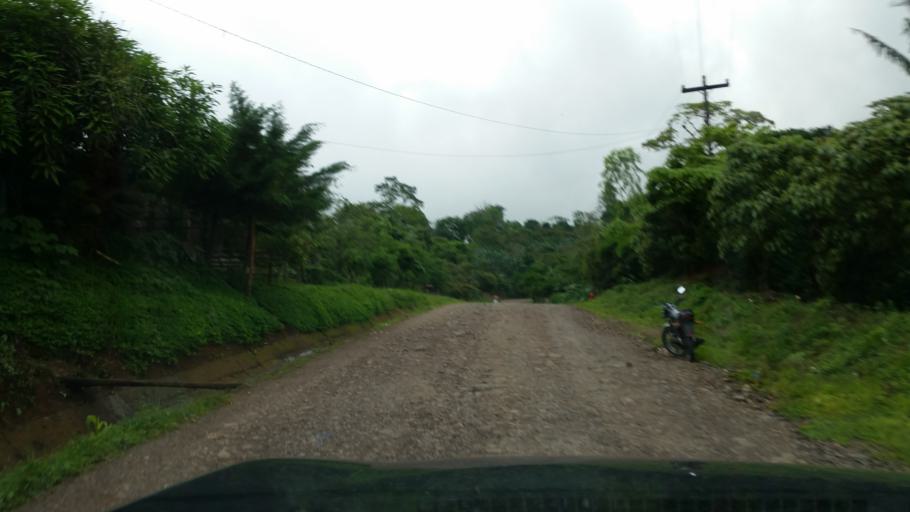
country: NI
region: Jinotega
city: Jinotega
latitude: 13.2750
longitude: -85.7282
